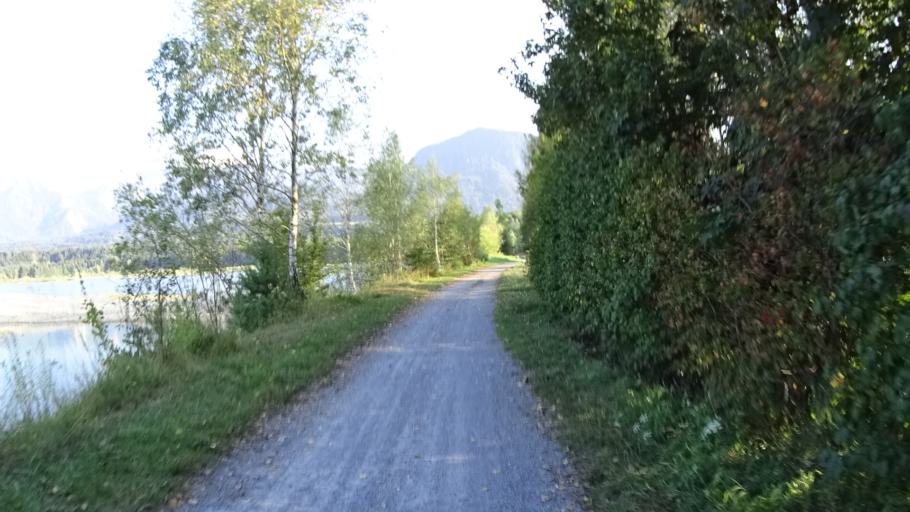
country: AT
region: Carinthia
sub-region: Politischer Bezirk Villach Land
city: Sankt Jakob
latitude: 46.5408
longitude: 14.0893
